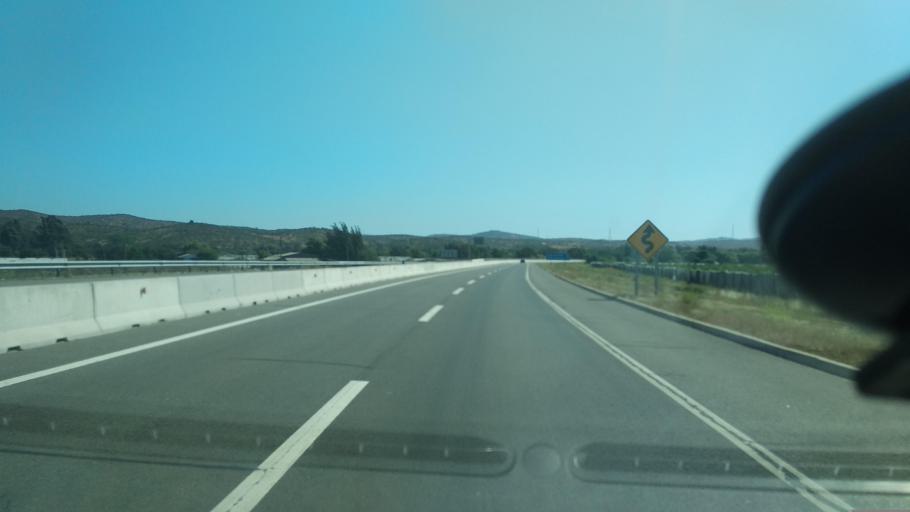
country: CL
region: Valparaiso
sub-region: Provincia de Marga Marga
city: Limache
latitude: -32.9781
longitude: -71.3056
